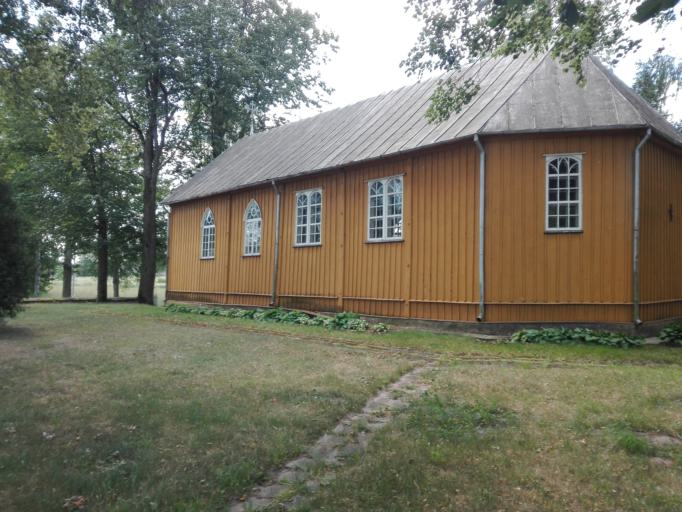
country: LT
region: Panevezys
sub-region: Birzai
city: Birzai
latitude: 56.1078
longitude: 24.8075
